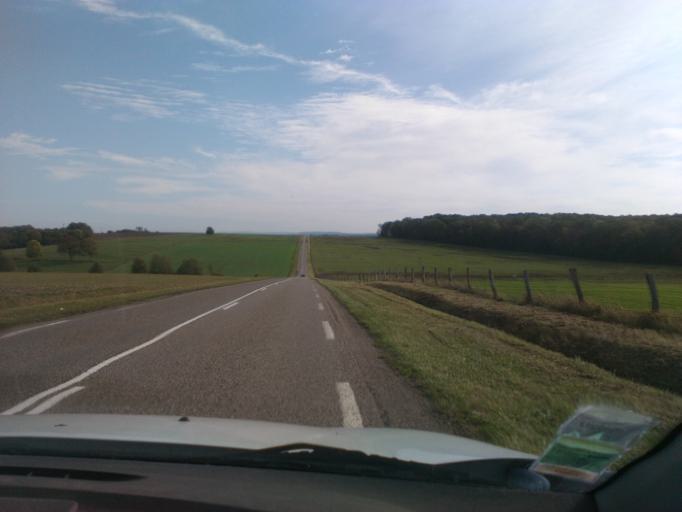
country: FR
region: Lorraine
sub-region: Departement des Vosges
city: Rambervillers
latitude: 48.3544
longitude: 6.5601
